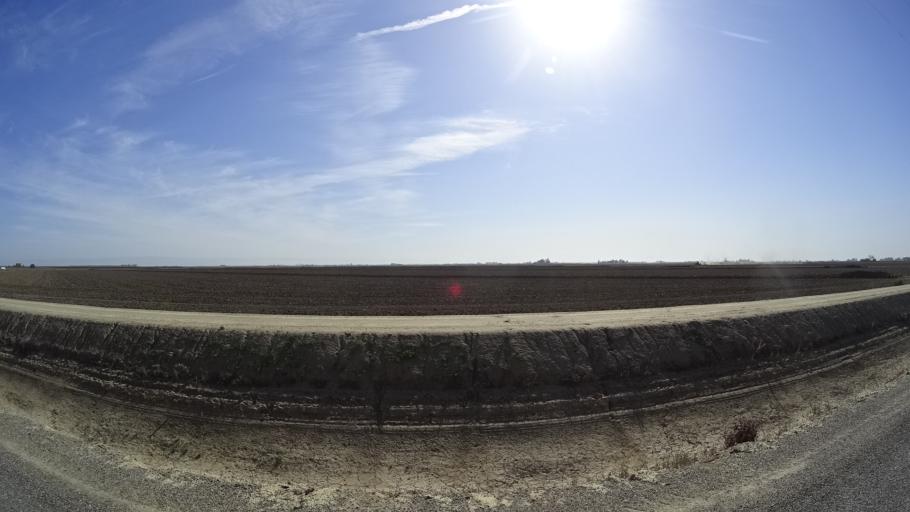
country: US
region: California
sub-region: Glenn County
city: Willows
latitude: 39.6072
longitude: -122.1169
